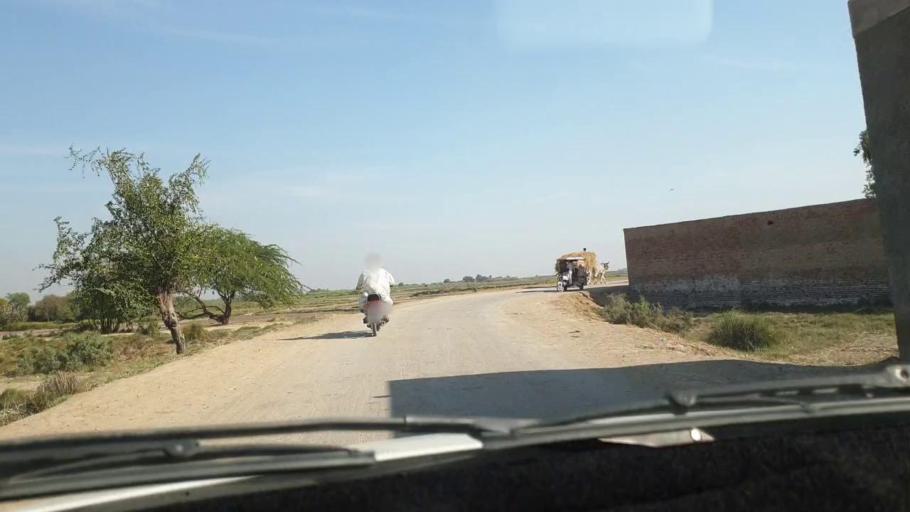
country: PK
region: Sindh
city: Bulri
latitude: 24.9565
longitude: 68.4204
